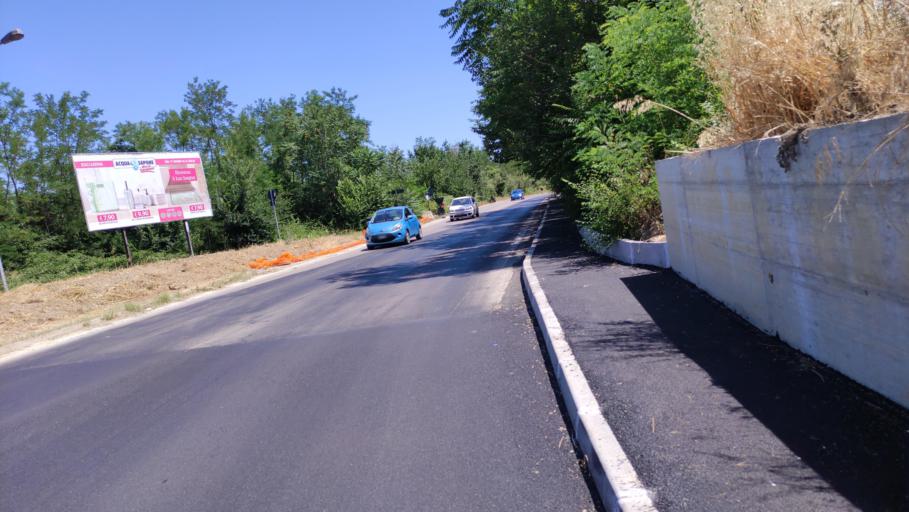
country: IT
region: Abruzzo
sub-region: Provincia di Chieti
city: Casalincontrada
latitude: 42.3264
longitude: 14.1013
